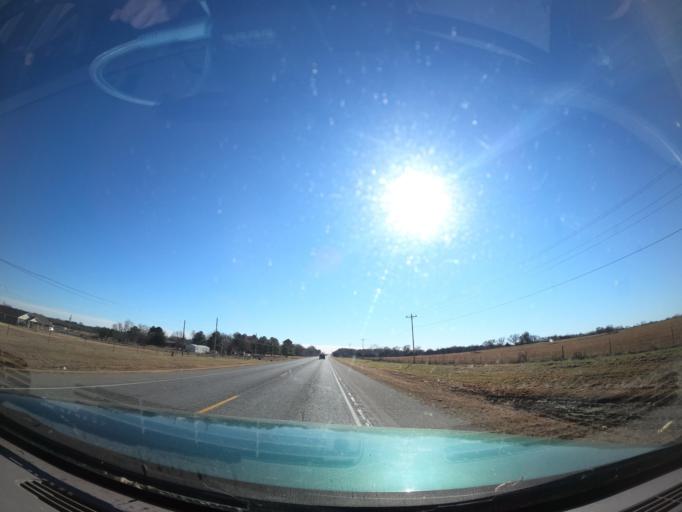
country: US
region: Oklahoma
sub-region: Muskogee County
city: Haskell
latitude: 35.8490
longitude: -95.6775
